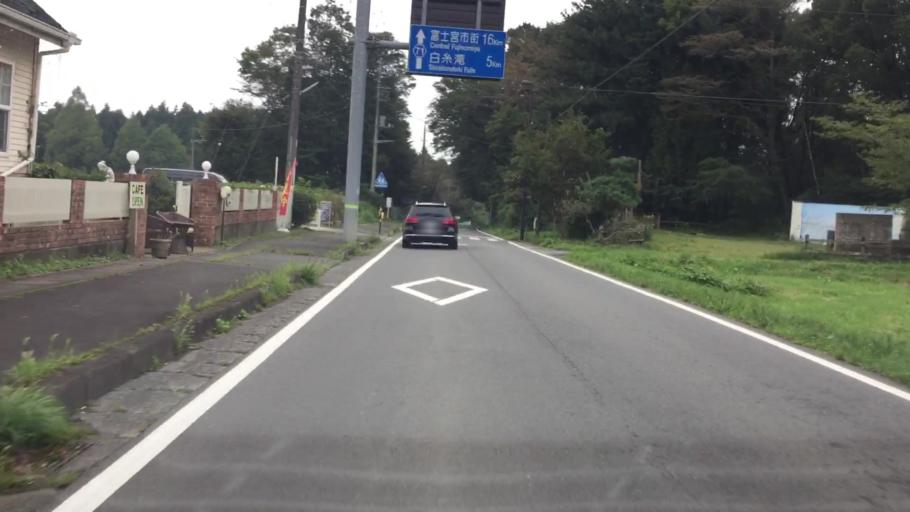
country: JP
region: Shizuoka
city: Fujinomiya
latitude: 35.3525
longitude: 138.5950
